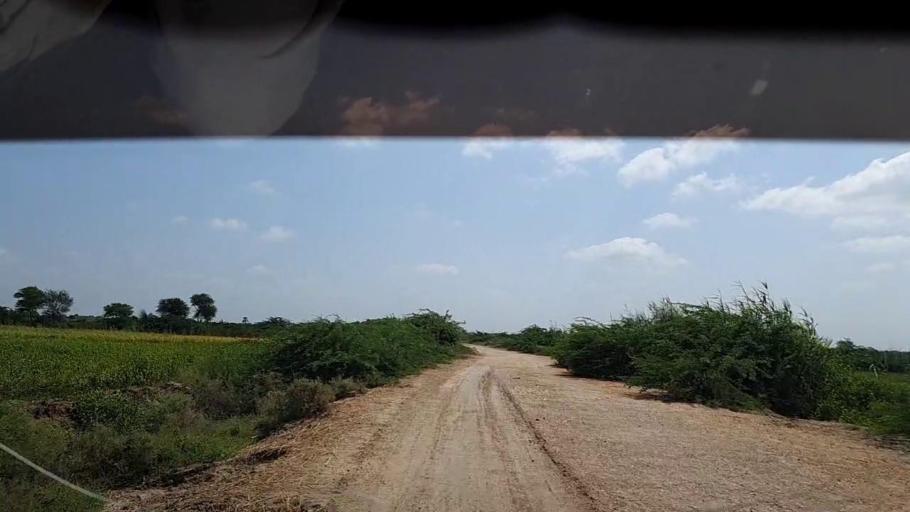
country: PK
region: Sindh
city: Kadhan
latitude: 24.6040
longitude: 68.9787
